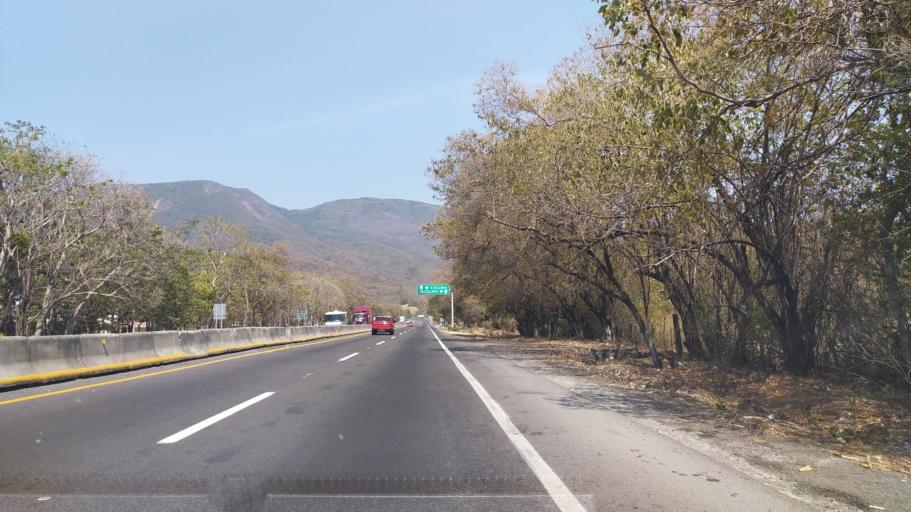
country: MX
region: Colima
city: Madrid
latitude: 19.0109
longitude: -103.8320
